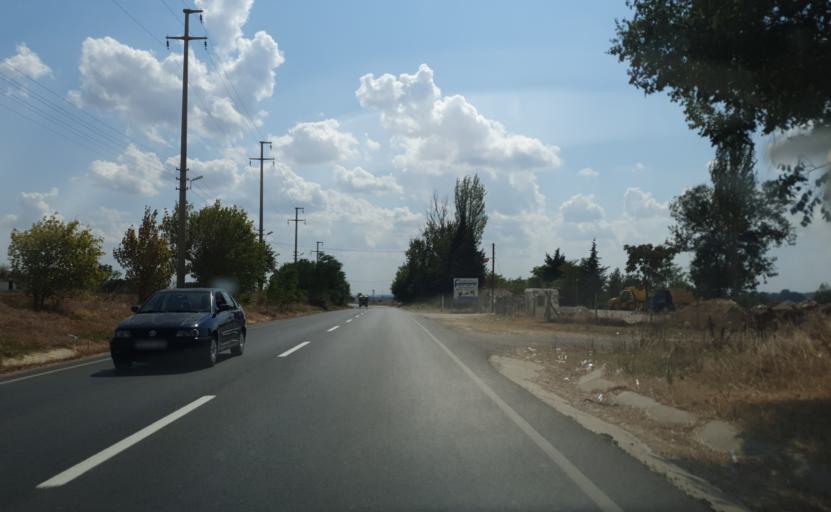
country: TR
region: Kirklareli
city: Luleburgaz
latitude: 41.3801
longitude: 27.3440
